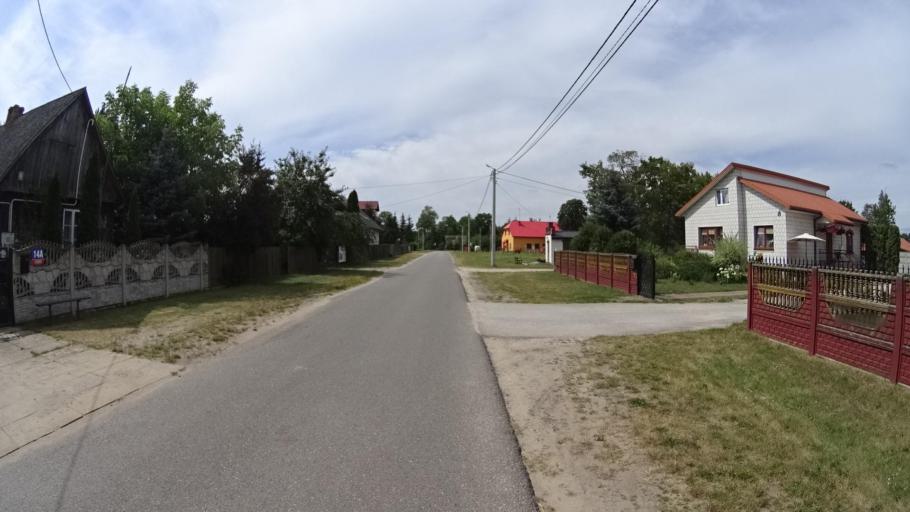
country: PL
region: Masovian Voivodeship
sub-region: Powiat bialobrzeski
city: Wysmierzyce
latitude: 51.6408
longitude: 20.8808
